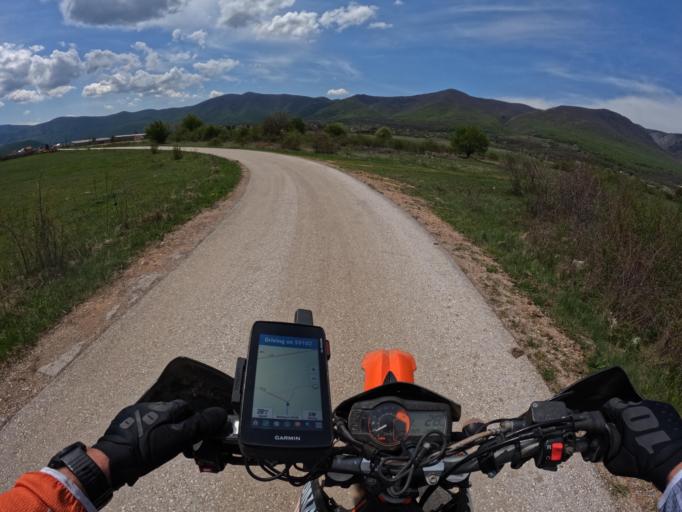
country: BA
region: Federation of Bosnia and Herzegovina
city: Orasac
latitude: 44.5660
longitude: 15.9453
